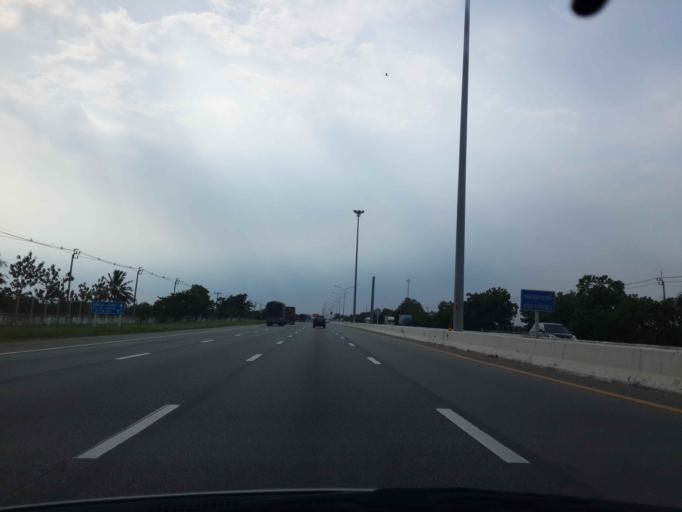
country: TH
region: Samut Prakan
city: Ban Khlong Bang Sao Thong
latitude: 13.6585
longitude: 100.8615
